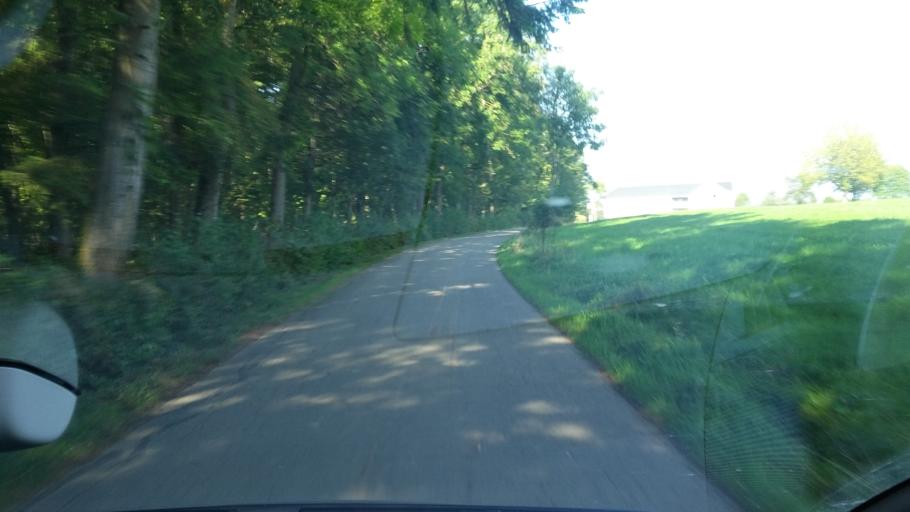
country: LU
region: Diekirch
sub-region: Canton de Redange
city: Beckerich
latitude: 49.7183
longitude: 5.8601
